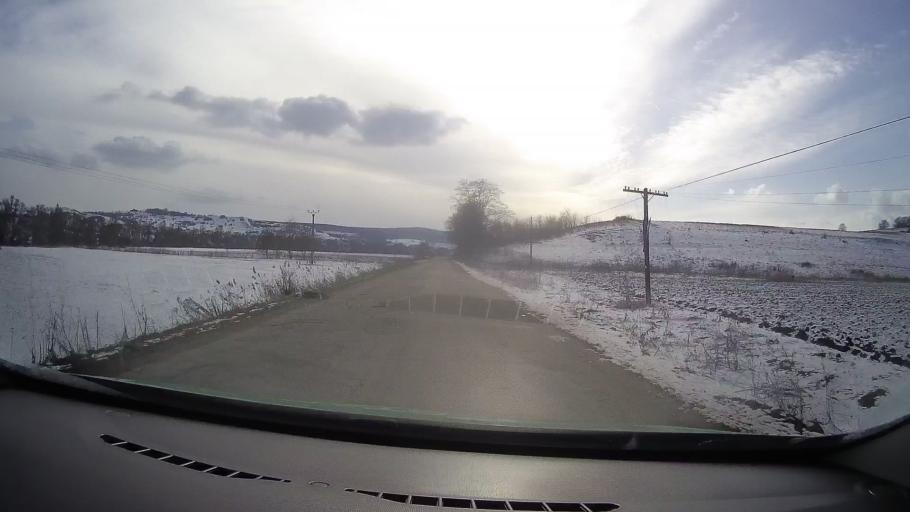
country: RO
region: Sibiu
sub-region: Comuna Iacobeni
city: Iacobeni
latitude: 46.0484
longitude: 24.7643
